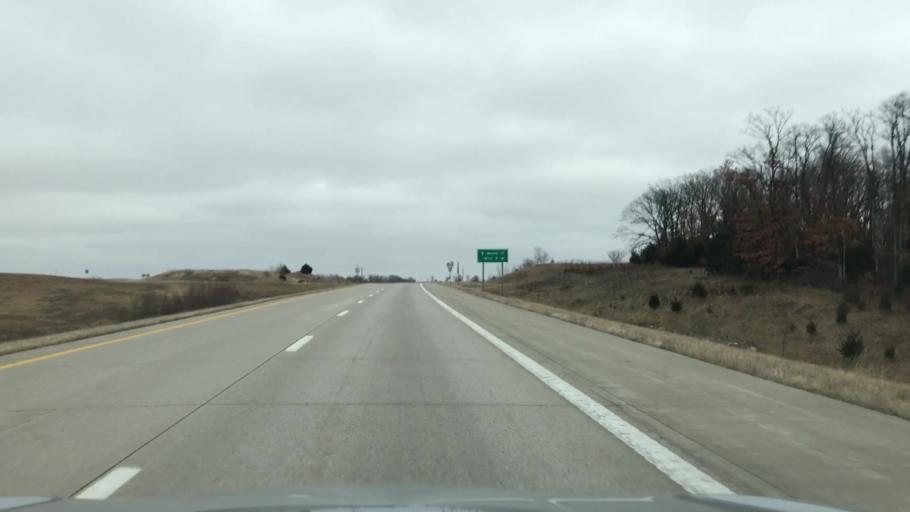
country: US
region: Missouri
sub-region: Linn County
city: Marceline
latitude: 39.7632
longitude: -92.7930
